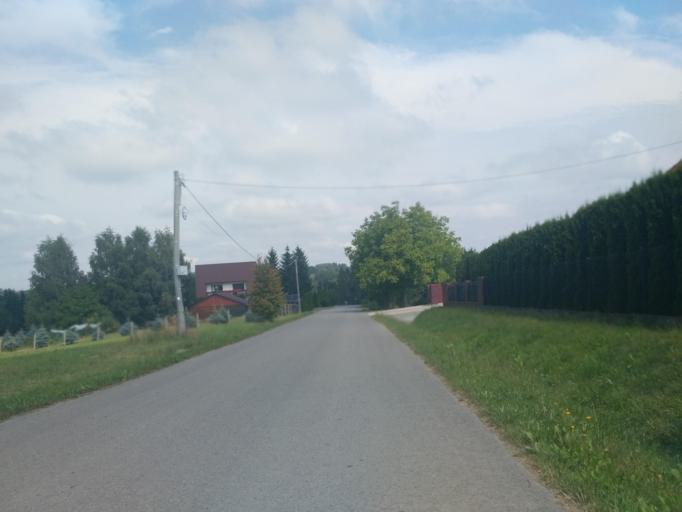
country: PL
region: Subcarpathian Voivodeship
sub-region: Powiat lancucki
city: Kraczkowa
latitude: 50.0330
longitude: 22.1674
